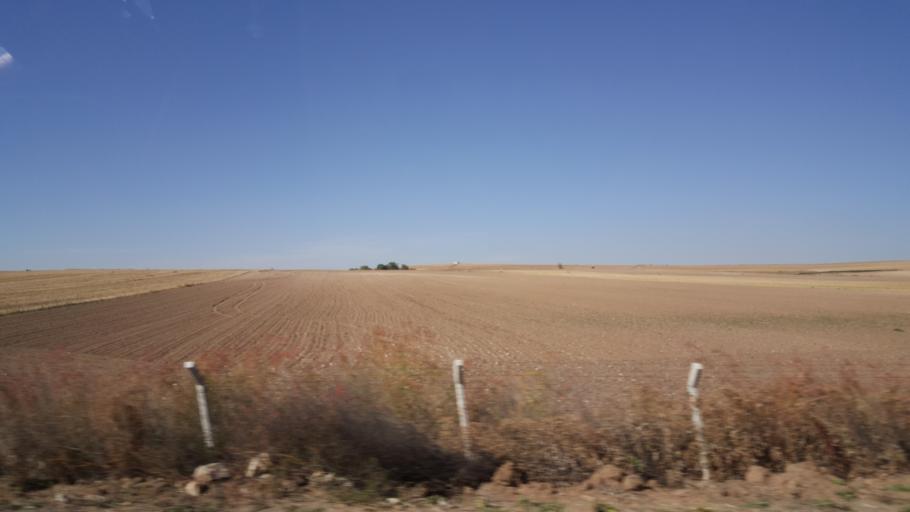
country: TR
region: Ankara
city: Ikizce
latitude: 39.6169
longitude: 32.6882
